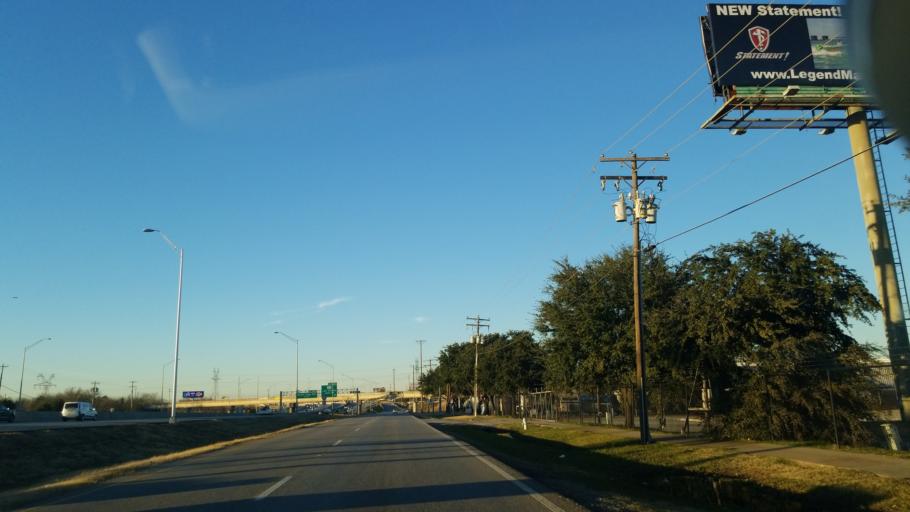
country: US
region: Texas
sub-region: Denton County
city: Lewisville
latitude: 33.0588
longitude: -97.0123
